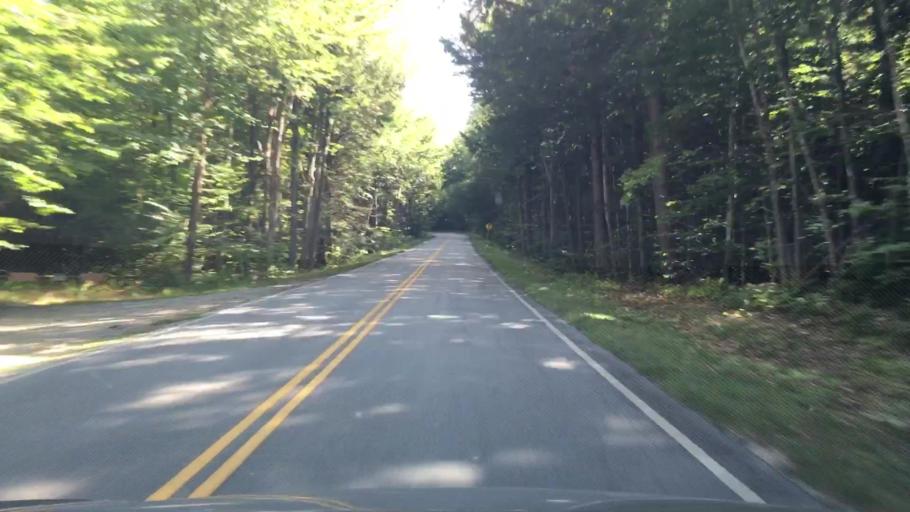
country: US
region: New Hampshire
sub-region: Carroll County
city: North Conway
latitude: 44.0662
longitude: -71.2823
